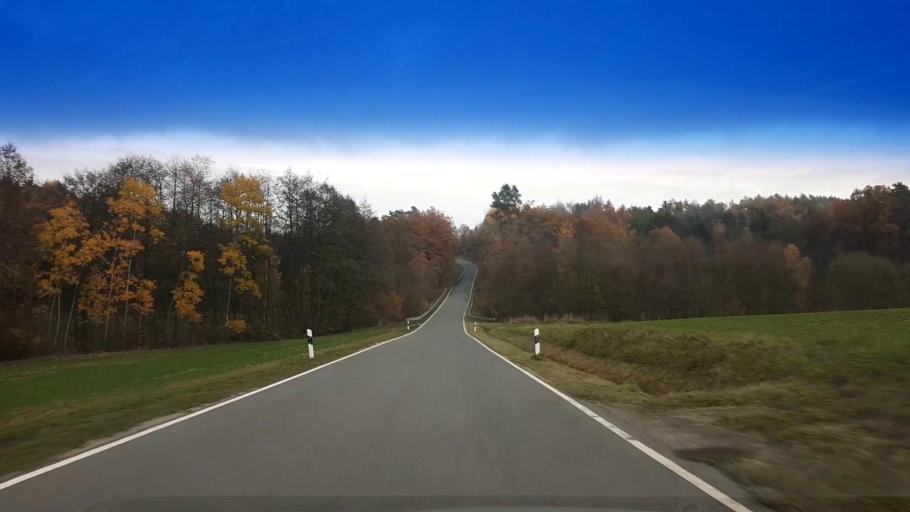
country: DE
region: Bavaria
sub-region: Upper Franconia
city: Zapfendorf
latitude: 50.0138
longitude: 10.9655
